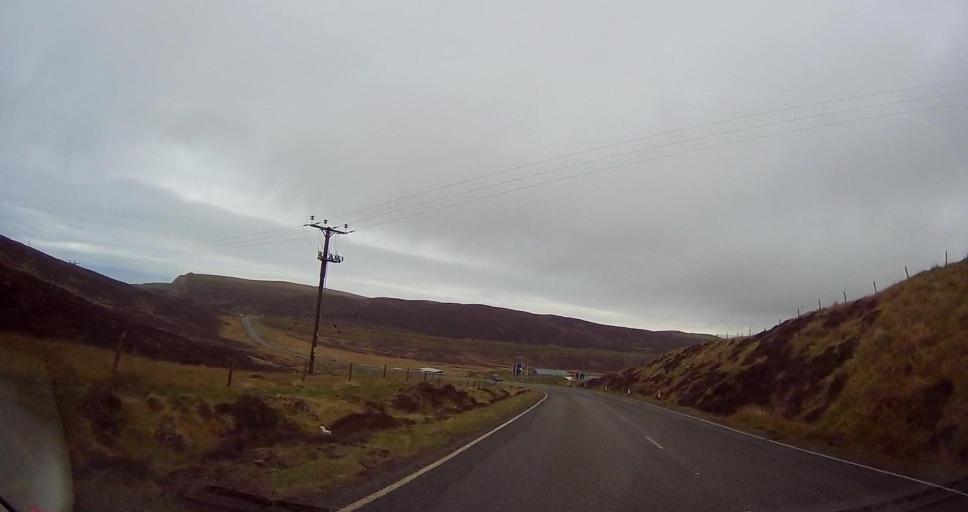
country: GB
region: Scotland
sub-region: Shetland Islands
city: Lerwick
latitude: 60.1390
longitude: -1.2344
